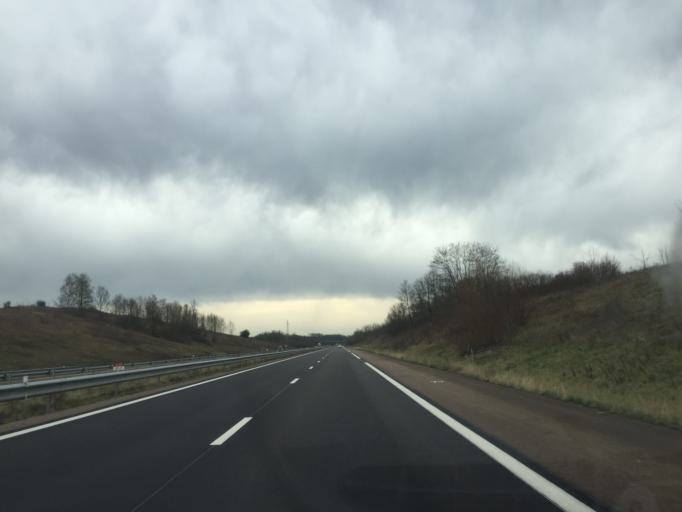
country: FR
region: Franche-Comte
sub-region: Departement du Jura
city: Bletterans
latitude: 46.7357
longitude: 5.5094
